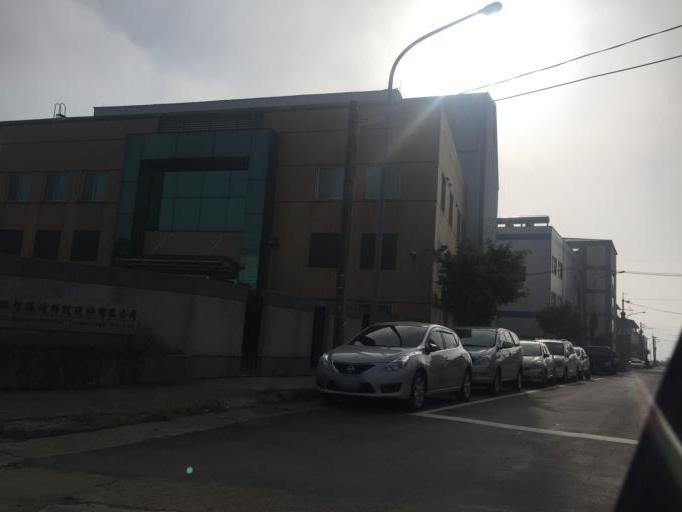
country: TW
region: Taiwan
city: Daxi
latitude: 24.8408
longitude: 121.2111
